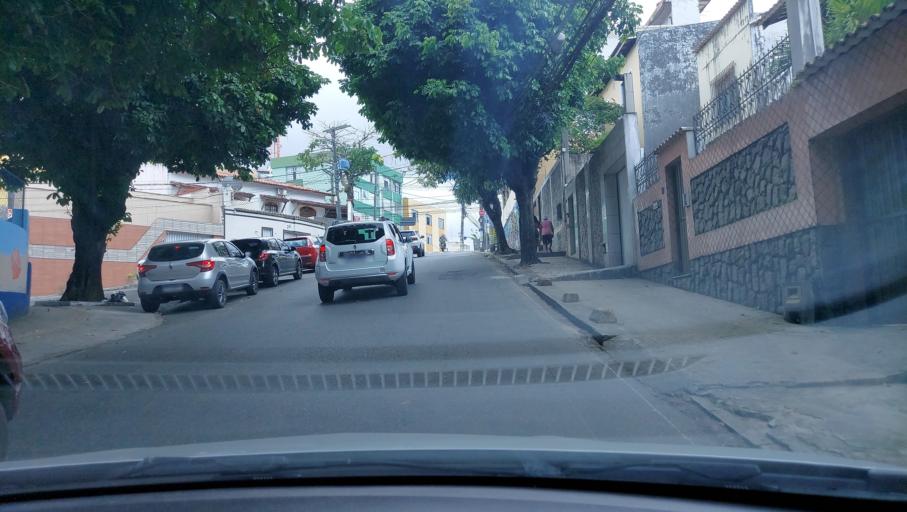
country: BR
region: Bahia
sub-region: Salvador
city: Salvador
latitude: -12.9719
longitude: -38.4906
